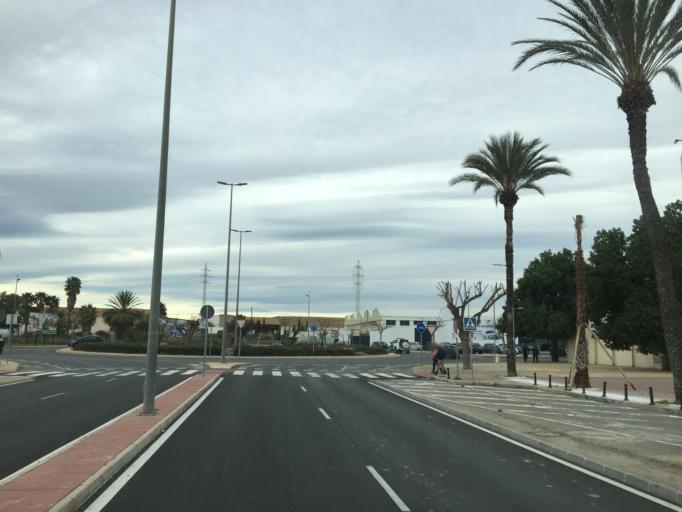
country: ES
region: Murcia
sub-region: Murcia
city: Cartagena
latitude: 37.6134
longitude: -1.0070
